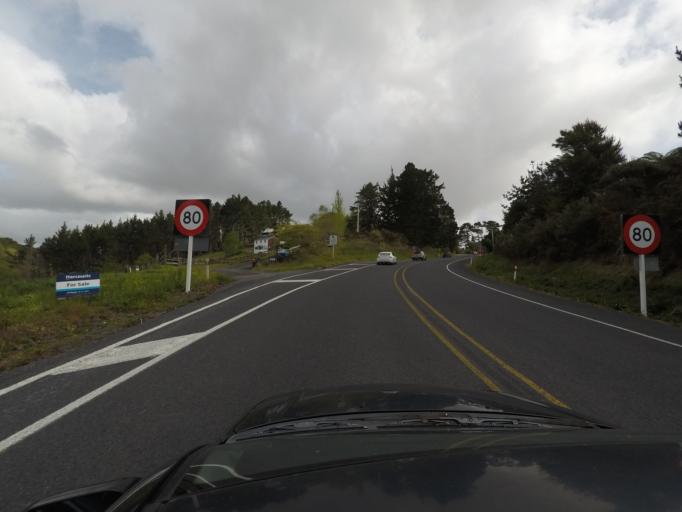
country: NZ
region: Auckland
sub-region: Auckland
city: Pakuranga
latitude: -36.9254
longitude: 174.9361
